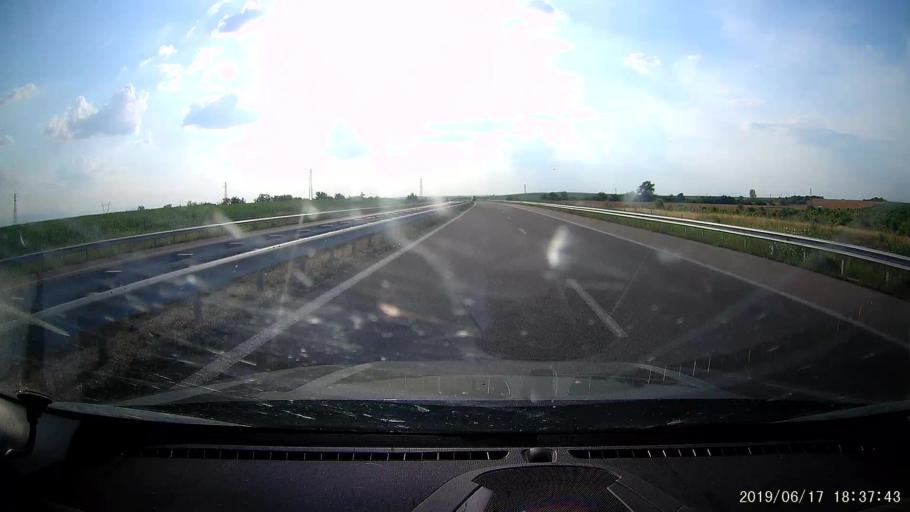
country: BG
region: Stara Zagora
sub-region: Obshtina Chirpan
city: Chirpan
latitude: 42.1330
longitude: 25.3538
